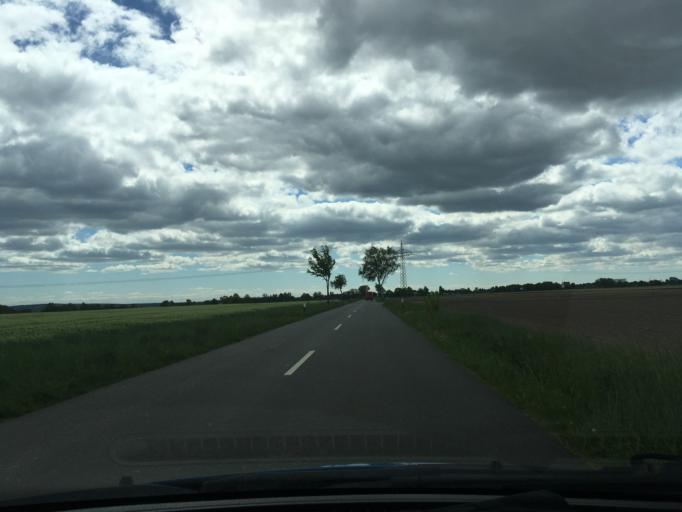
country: DE
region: Lower Saxony
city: Suderburg
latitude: 52.9186
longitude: 10.4390
